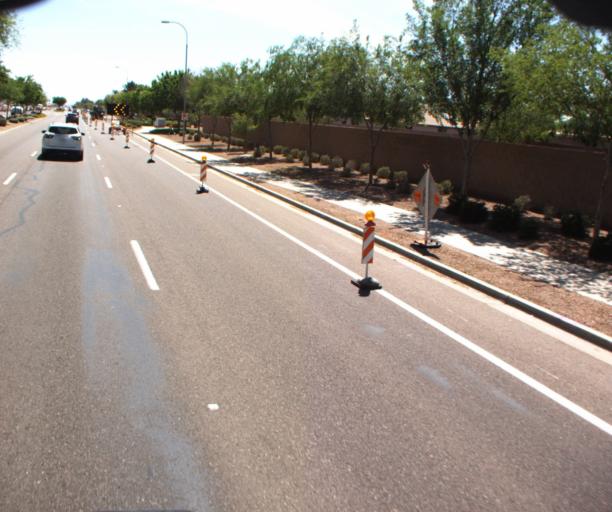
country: US
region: Arizona
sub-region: Maricopa County
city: Sun Lakes
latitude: 33.2369
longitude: -111.8413
